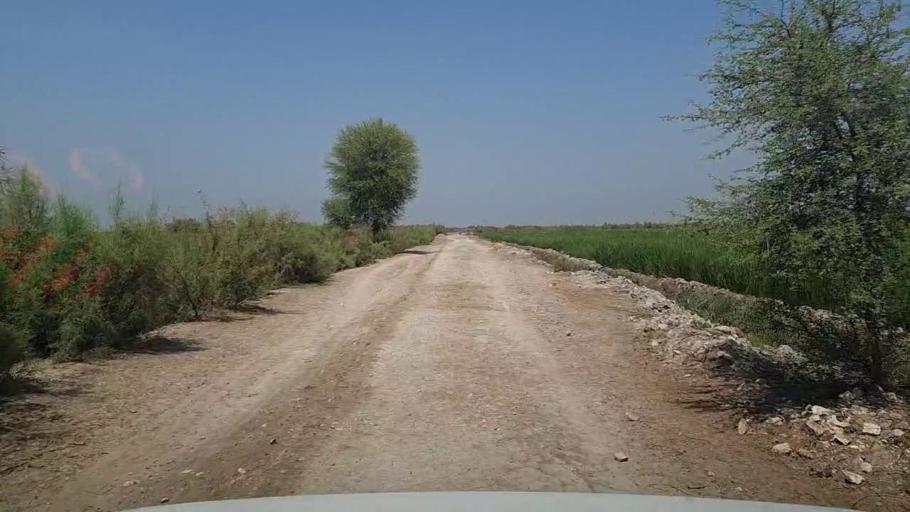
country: PK
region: Sindh
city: Kandhkot
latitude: 28.3412
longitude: 69.3025
